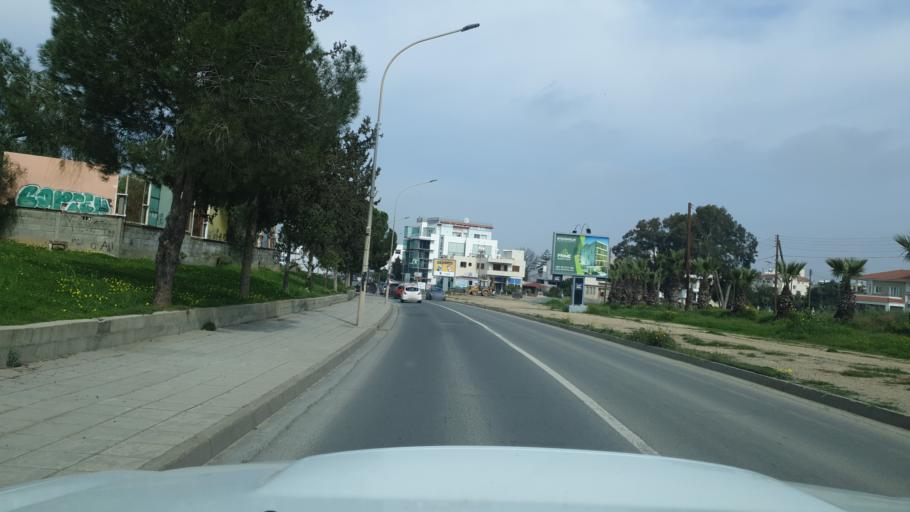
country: CY
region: Lefkosia
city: Nicosia
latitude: 35.1528
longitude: 33.3173
